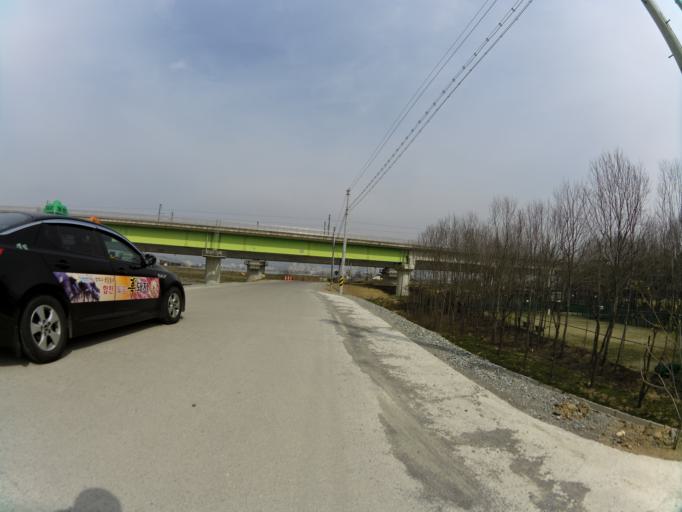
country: KR
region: Gyeongsangbuk-do
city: Gyeongsan-si
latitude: 35.8535
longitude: 128.7090
